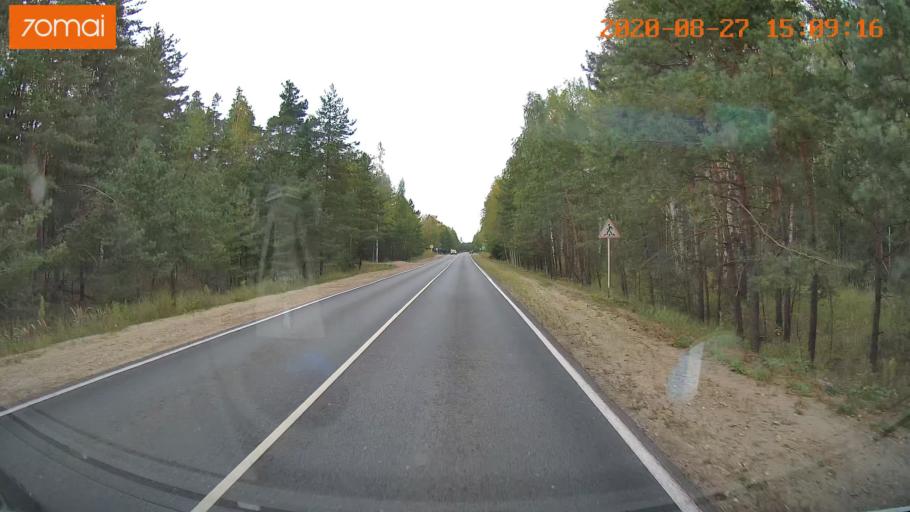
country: RU
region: Vladimir
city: Kurlovo
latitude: 55.5027
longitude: 40.5722
